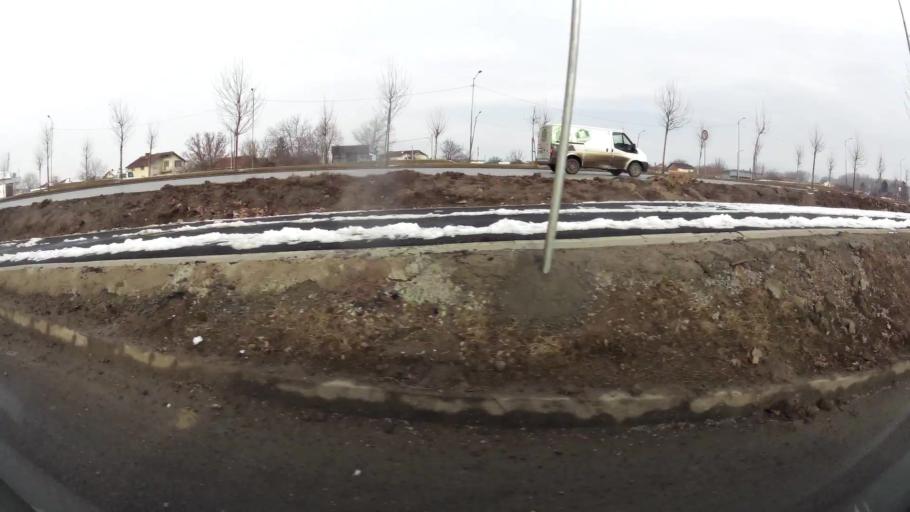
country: BG
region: Sofia-Capital
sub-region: Stolichna Obshtina
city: Sofia
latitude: 42.7083
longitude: 23.4168
